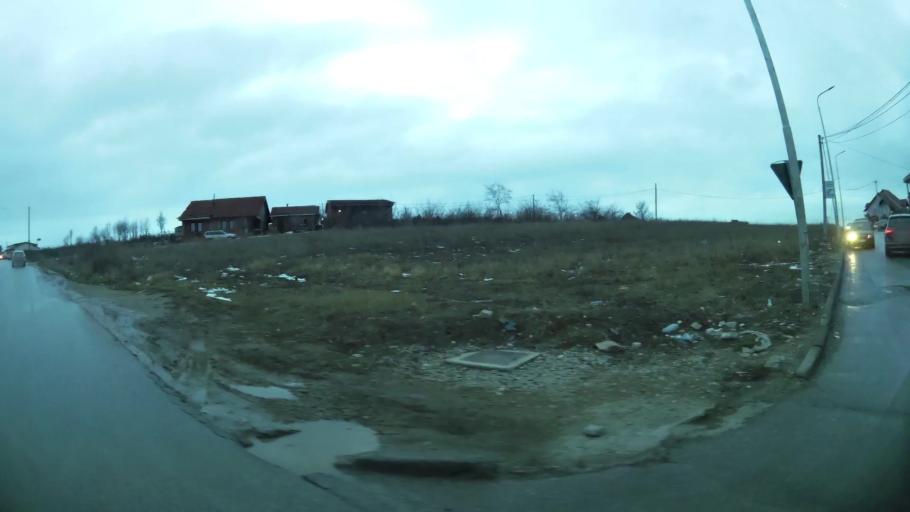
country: XK
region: Pristina
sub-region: Komuna e Prishtines
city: Pristina
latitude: 42.6318
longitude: 21.1686
